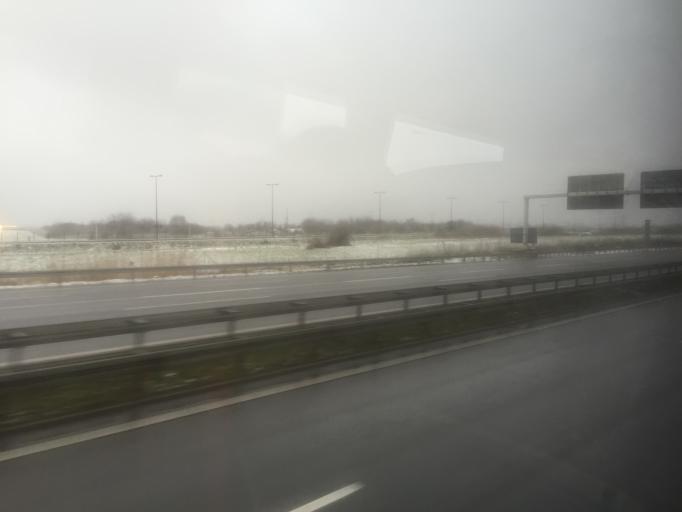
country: DE
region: Brandenburg
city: Schonefeld
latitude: 52.3807
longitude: 13.5405
